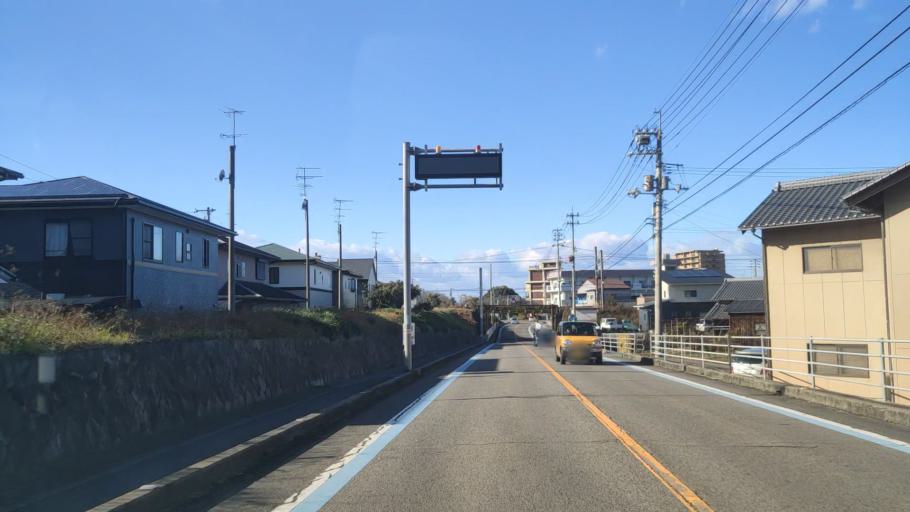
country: JP
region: Ehime
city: Saijo
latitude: 33.9087
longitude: 133.1833
